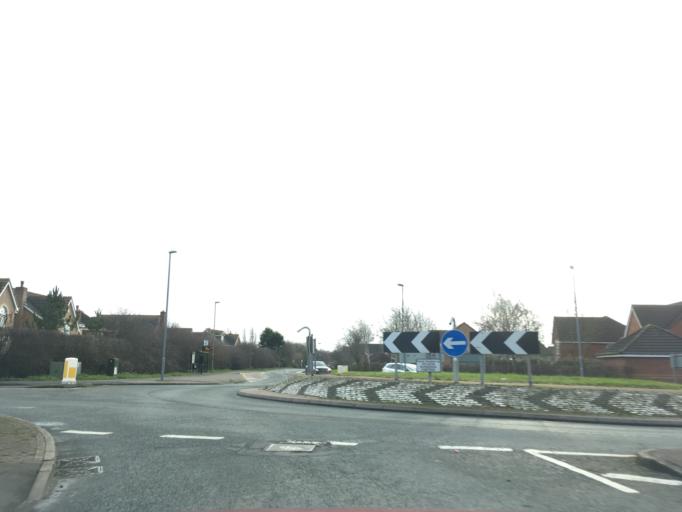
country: GB
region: England
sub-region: Nottinghamshire
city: East Leake
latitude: 52.8365
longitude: -1.1784
